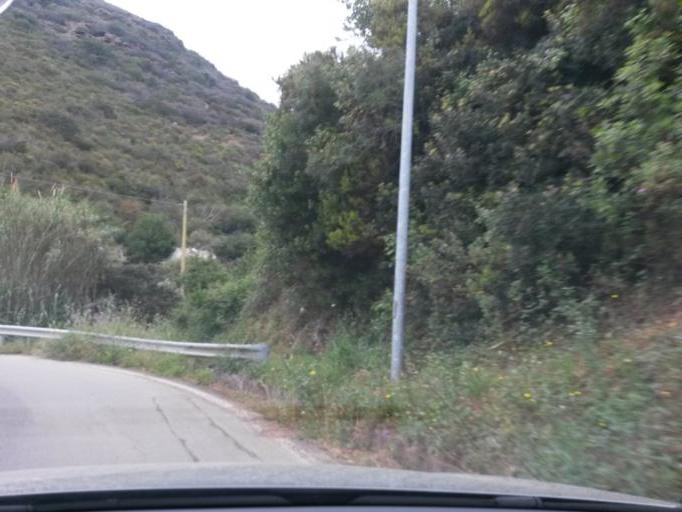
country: IT
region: Tuscany
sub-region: Provincia di Livorno
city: Capoliveri
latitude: 42.7267
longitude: 10.3795
